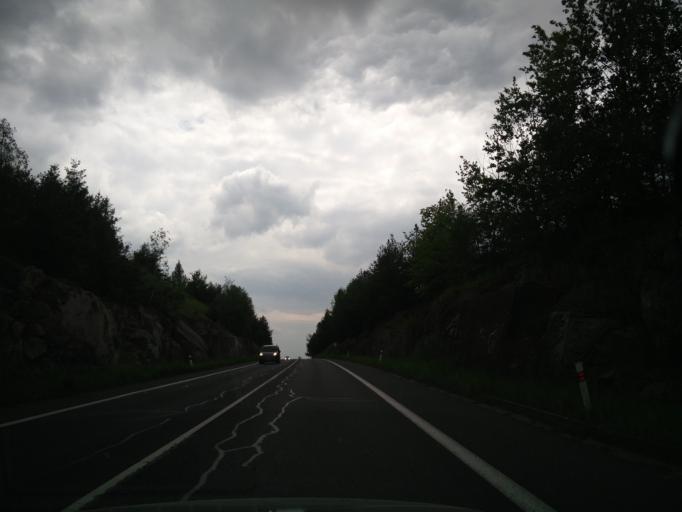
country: CZ
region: Central Bohemia
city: Milin
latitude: 49.6274
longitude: 14.0515
